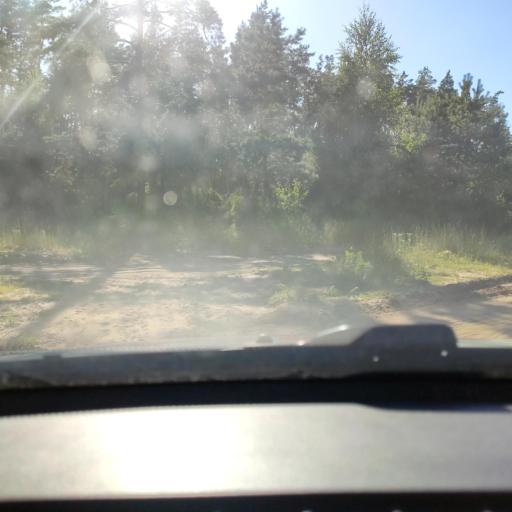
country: RU
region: Voronezj
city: Pridonskoy
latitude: 51.6314
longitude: 39.0855
